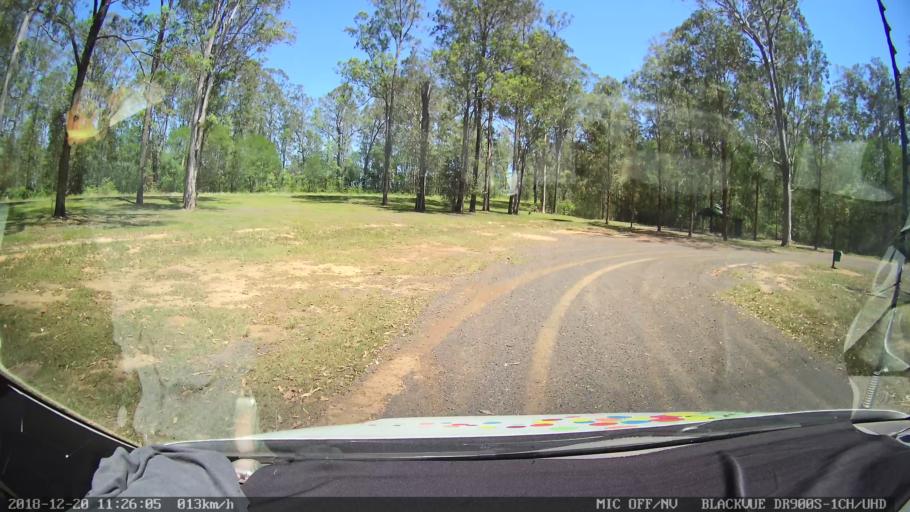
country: AU
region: New South Wales
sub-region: Richmond Valley
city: Casino
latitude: -29.0879
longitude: 153.0016
